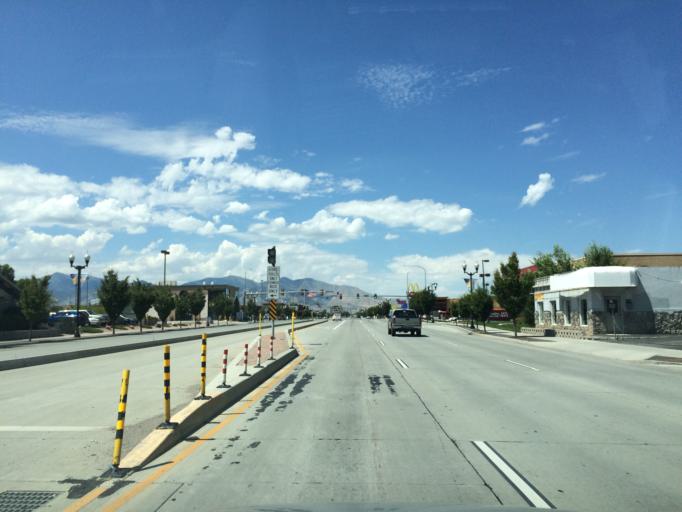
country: US
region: Utah
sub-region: Salt Lake County
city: West Valley City
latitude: 40.6967
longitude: -111.9716
